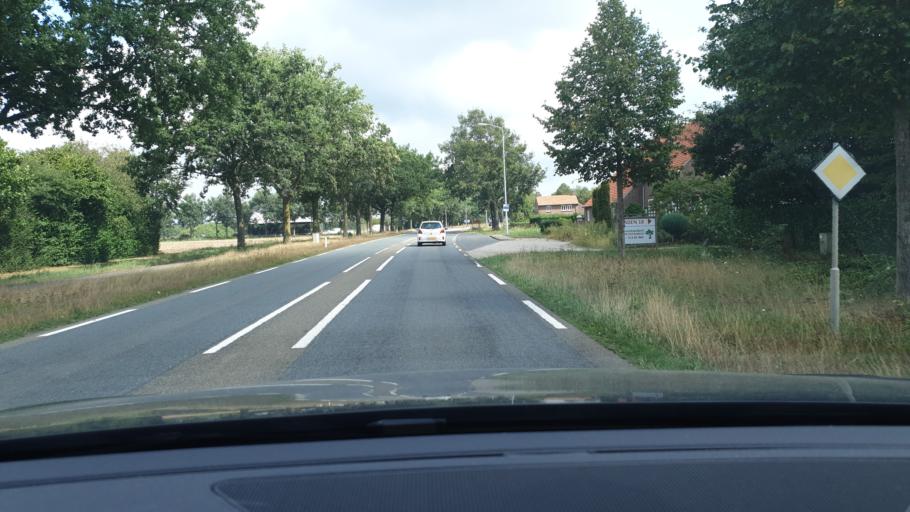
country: NL
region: North Brabant
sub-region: Gemeente Oirschot
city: Oostelbeers
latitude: 51.4887
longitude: 5.2864
